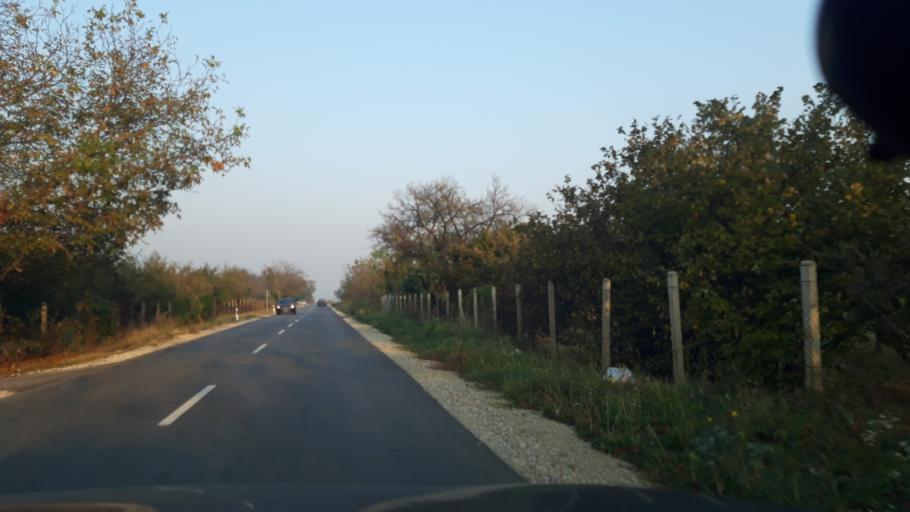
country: RS
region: Autonomna Pokrajina Vojvodina
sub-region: Juznobacki Okrug
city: Sremski Karlovci
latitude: 45.1532
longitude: 19.9527
